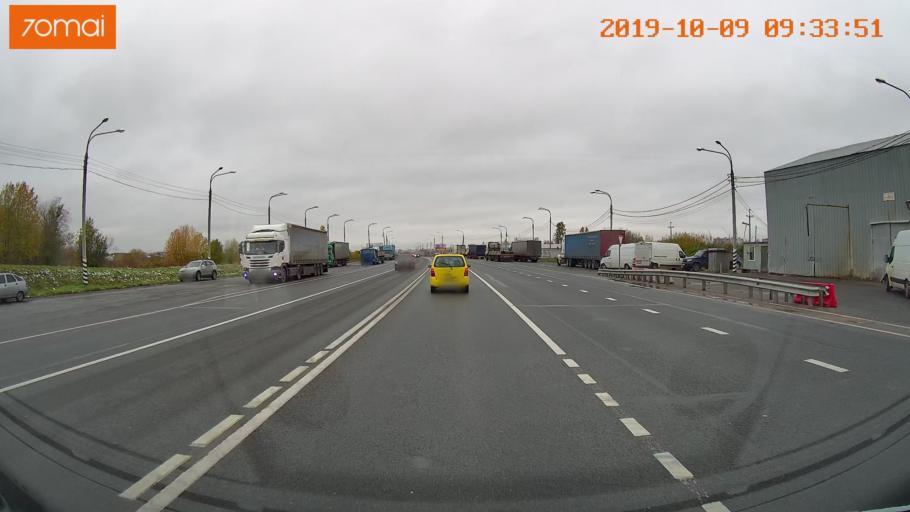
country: RU
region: Vologda
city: Vologda
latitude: 59.1712
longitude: 39.9083
